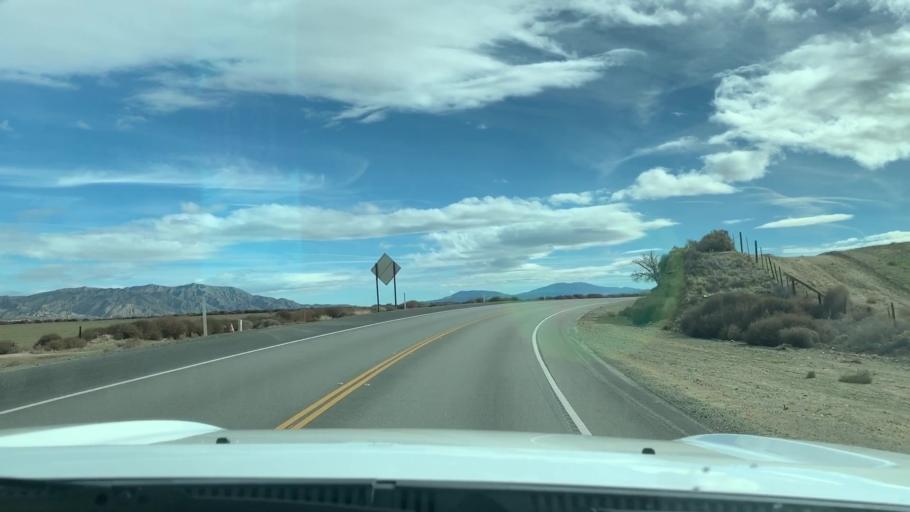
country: US
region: California
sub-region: Kern County
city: Taft Heights
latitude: 34.9635
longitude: -119.7232
